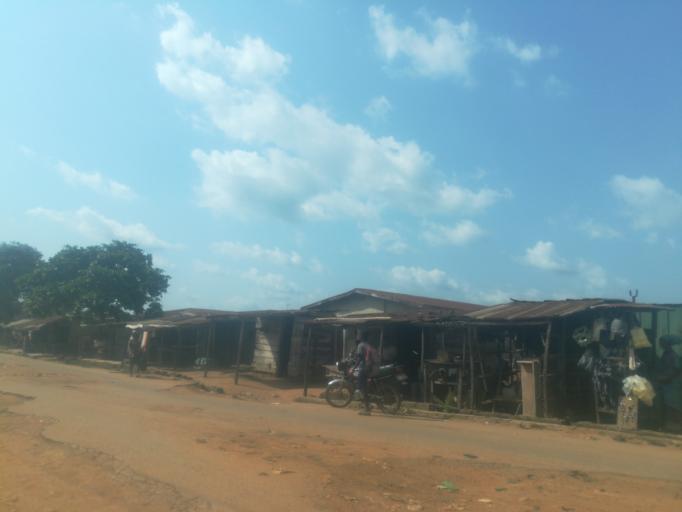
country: NG
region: Oyo
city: Moniya
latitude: 7.5252
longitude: 3.9104
